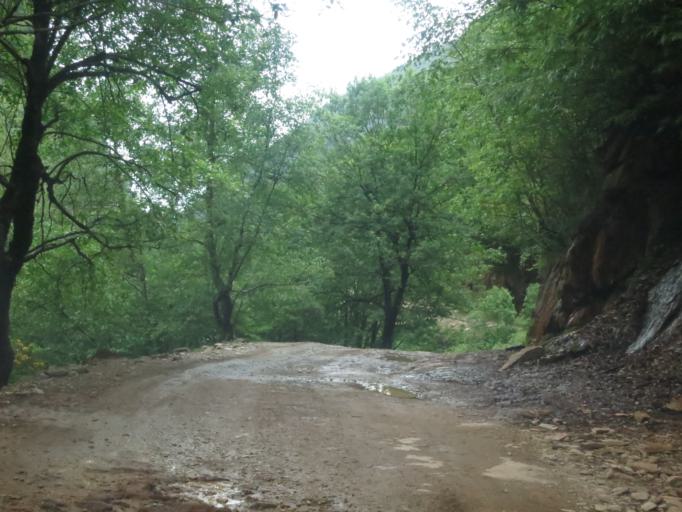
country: GE
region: Kakheti
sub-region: Telavi
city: Telavi
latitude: 42.2305
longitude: 45.4854
